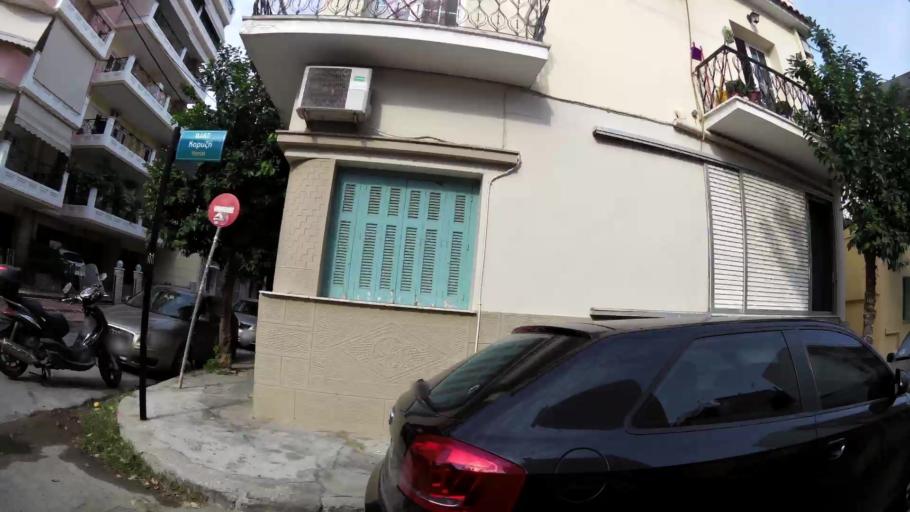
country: GR
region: Attica
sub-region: Nomarchia Athinas
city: Tavros
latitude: 37.9669
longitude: 23.7009
